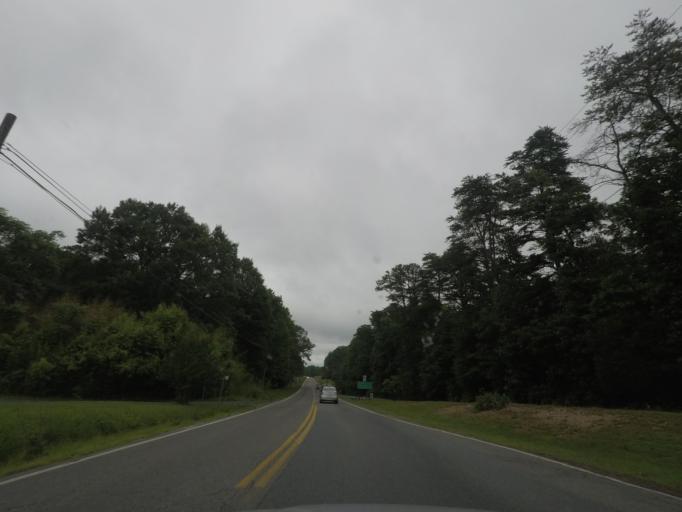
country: US
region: Virginia
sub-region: Fluvanna County
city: Weber City
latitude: 37.7825
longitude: -78.2353
